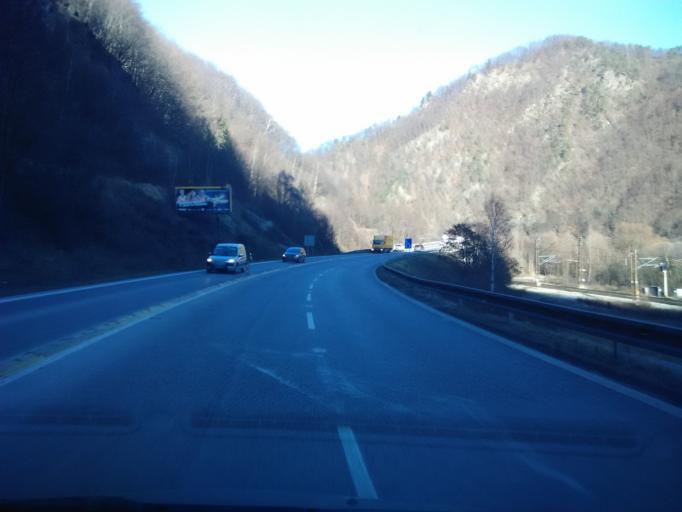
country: SK
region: Zilinsky
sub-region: Okres Zilina
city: Vrutky
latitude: 49.1564
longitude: 18.8844
